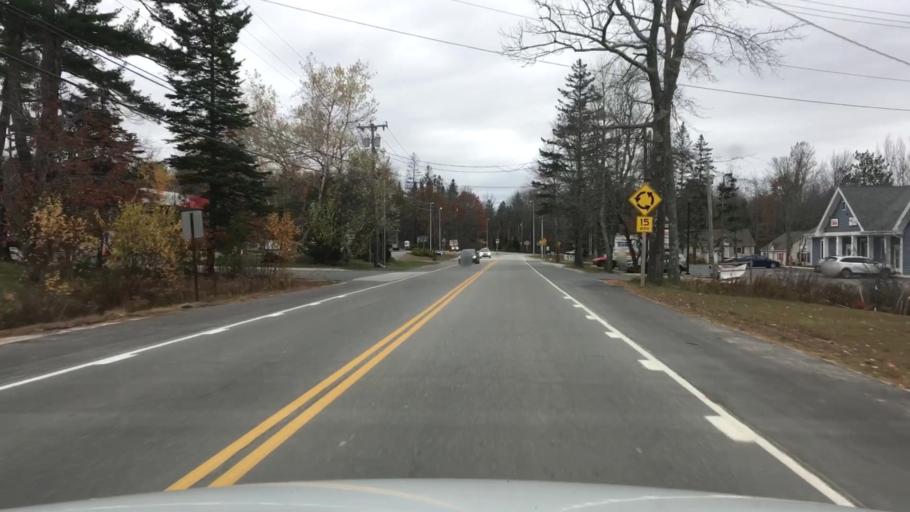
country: US
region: Maine
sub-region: Hancock County
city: Sedgwick
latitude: 44.4067
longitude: -68.5958
